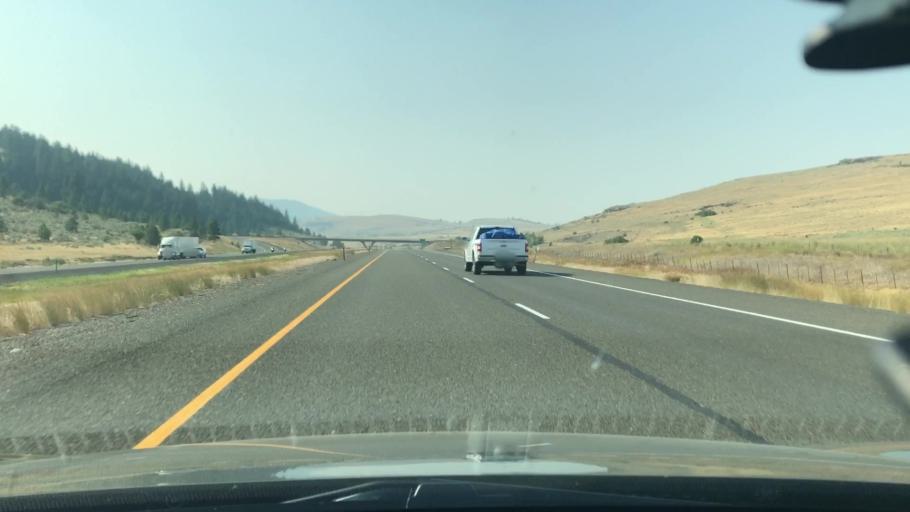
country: US
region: Oregon
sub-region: Union County
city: Union
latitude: 45.1787
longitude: -117.9825
